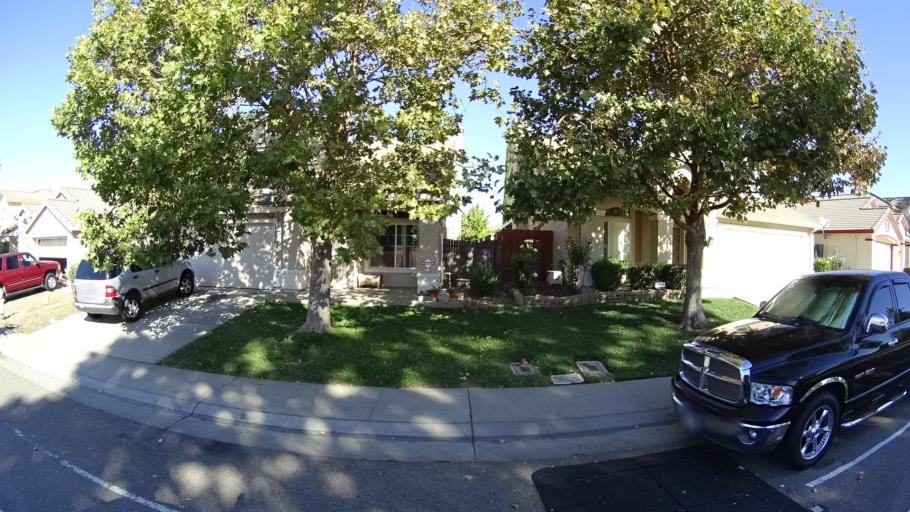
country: US
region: California
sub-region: Sacramento County
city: Vineyard
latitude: 38.4470
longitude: -121.3607
